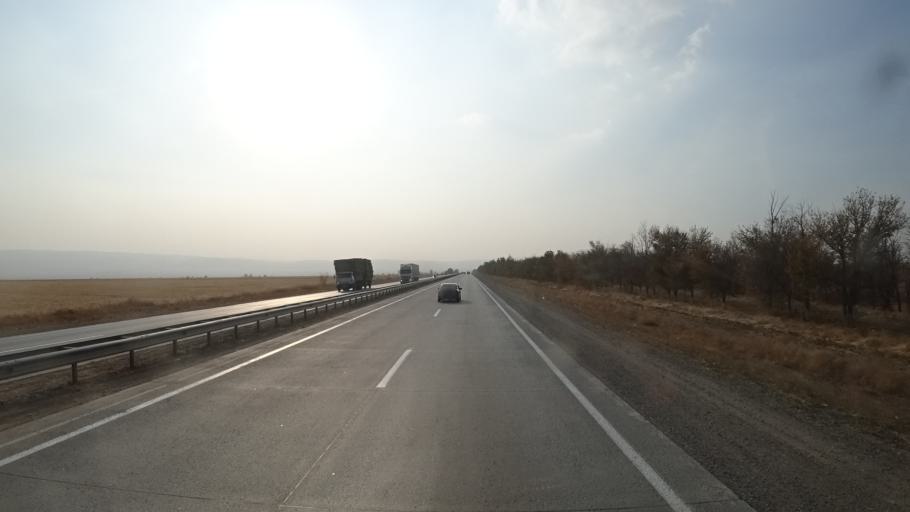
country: KZ
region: Zhambyl
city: Taraz
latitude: 42.8037
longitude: 71.1061
